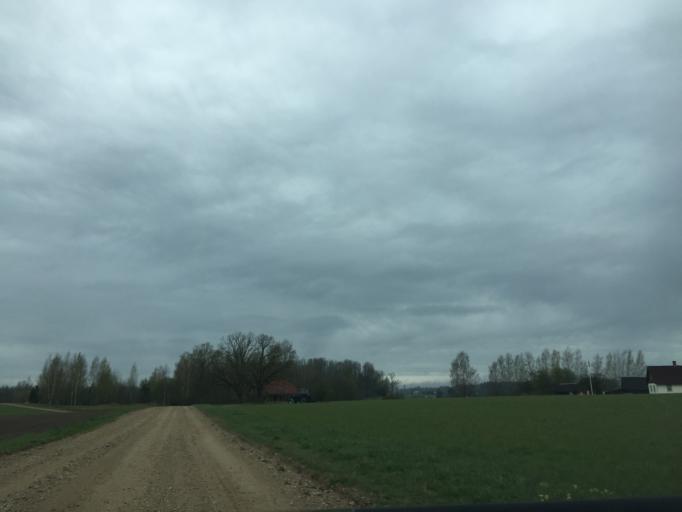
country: LV
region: Sigulda
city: Sigulda
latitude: 57.0350
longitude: 24.8454
